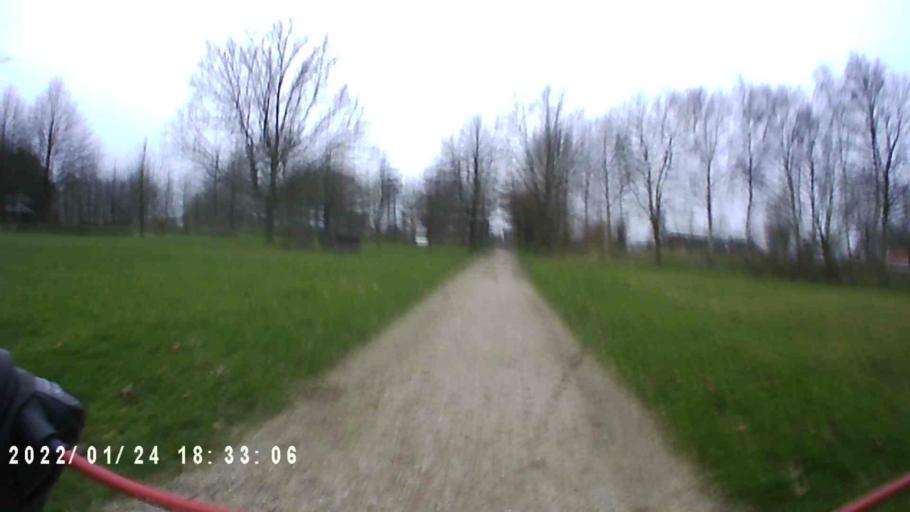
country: NL
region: Groningen
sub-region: Gemeente De Marne
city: Ulrum
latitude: 53.3574
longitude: 6.3351
